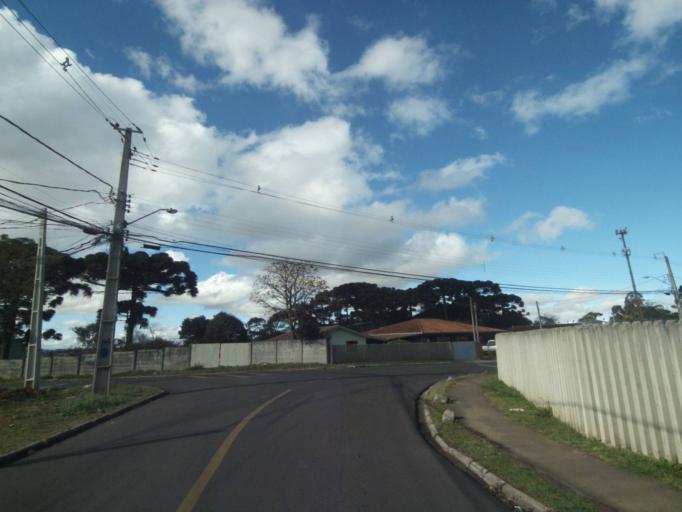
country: BR
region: Parana
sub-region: Sao Jose Dos Pinhais
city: Sao Jose dos Pinhais
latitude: -25.5283
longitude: -49.2842
